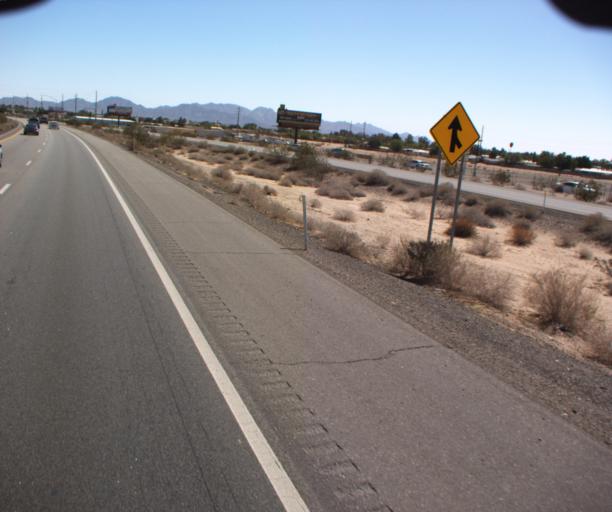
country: US
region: Arizona
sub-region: Yuma County
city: Fortuna Foothills
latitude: 32.6707
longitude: -114.4818
